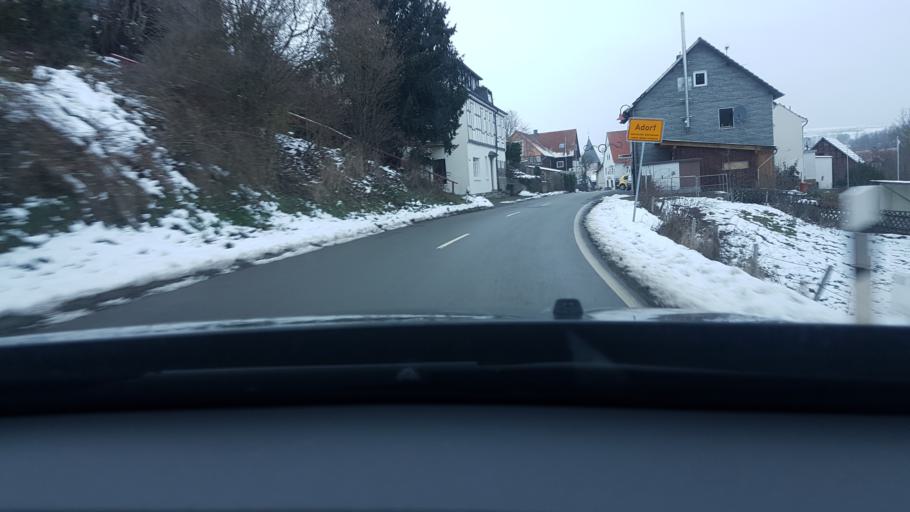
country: DE
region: Hesse
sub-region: Regierungsbezirk Kassel
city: Korbach
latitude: 51.3578
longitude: 8.8069
